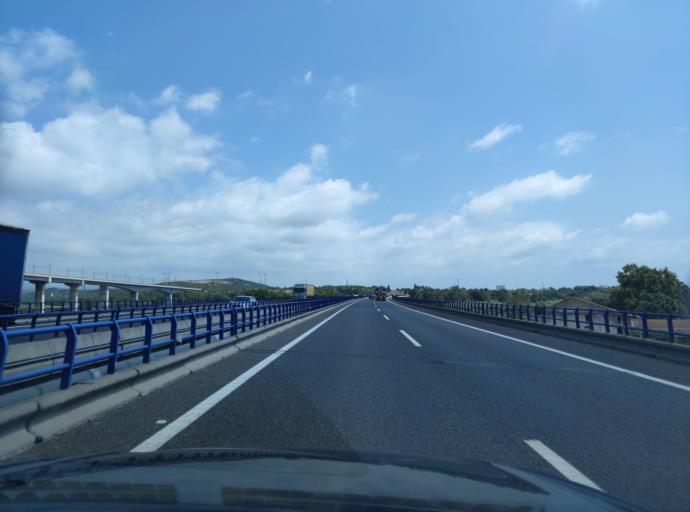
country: ES
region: Catalonia
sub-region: Provincia de Tarragona
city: Amposta
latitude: 40.7258
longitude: 0.5708
